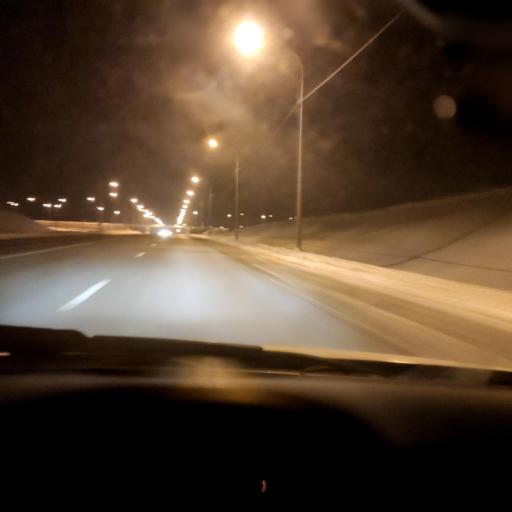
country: RU
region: Kursk
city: Fatezh
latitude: 52.0949
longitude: 35.8203
